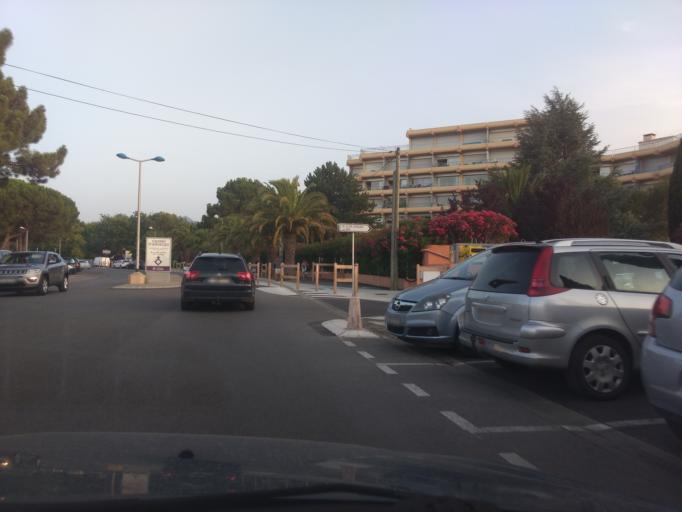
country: FR
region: Languedoc-Roussillon
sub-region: Departement des Pyrenees-Orientales
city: Argelers
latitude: 42.5541
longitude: 3.0430
